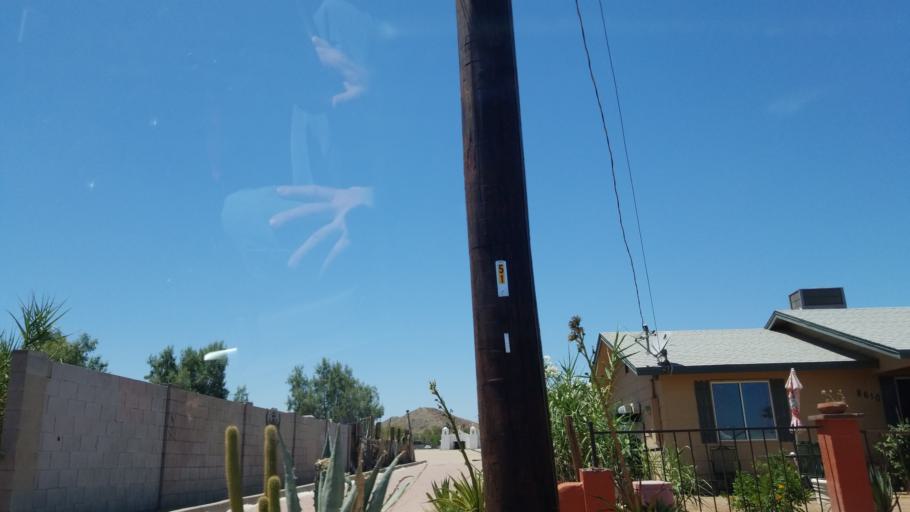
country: US
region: Arizona
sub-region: Maricopa County
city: Guadalupe
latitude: 33.3685
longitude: -111.9632
